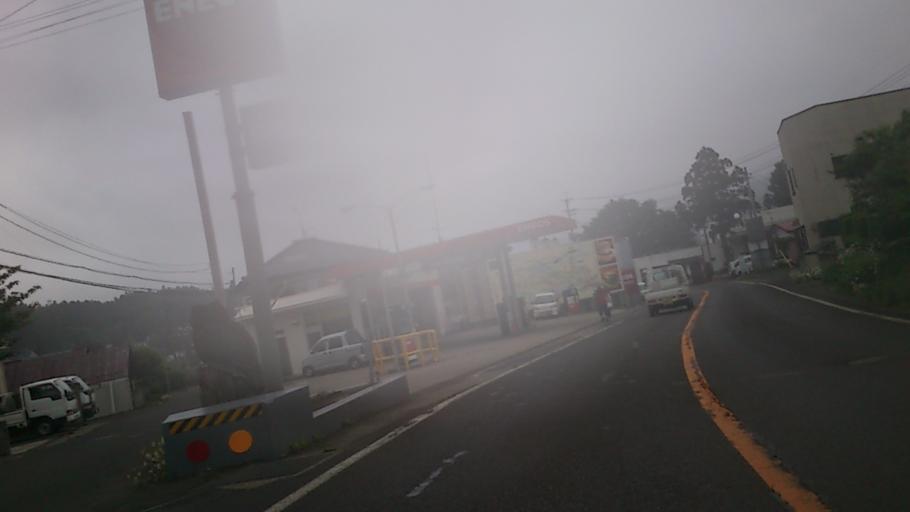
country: JP
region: Miyagi
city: Shiroishi
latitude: 38.1240
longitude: 140.5742
